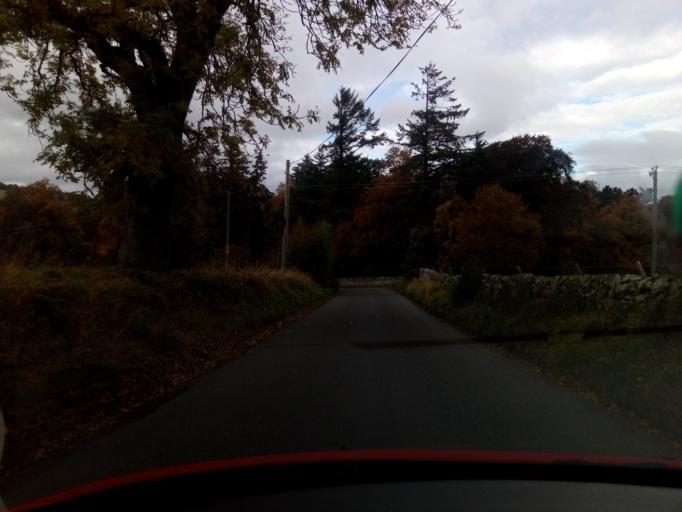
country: GB
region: Scotland
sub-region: The Scottish Borders
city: Peebles
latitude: 55.6327
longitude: -3.1415
